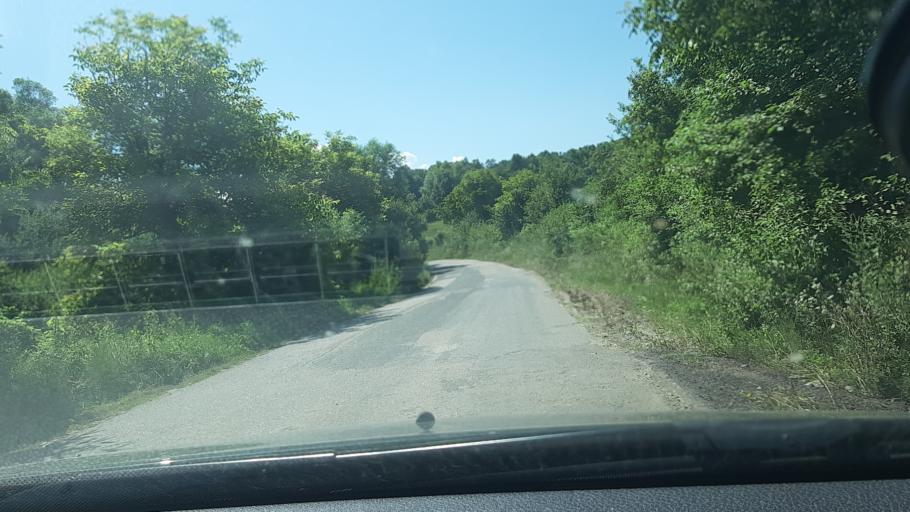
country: RO
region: Hunedoara
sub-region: Comuna Teliucu Inferior
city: Teliucu Inferior
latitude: 45.6847
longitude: 22.8712
